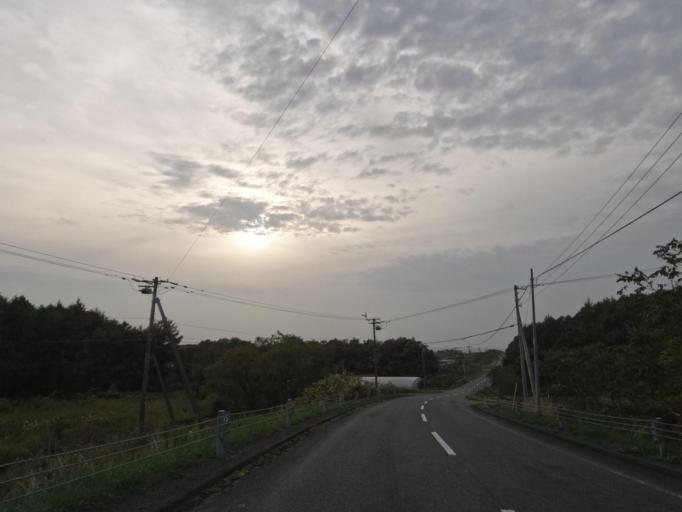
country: JP
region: Hokkaido
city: Date
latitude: 42.4173
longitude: 140.9229
